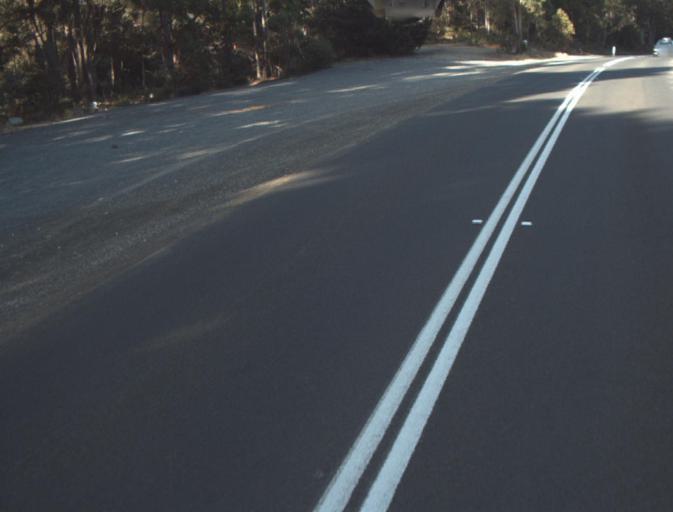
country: AU
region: Tasmania
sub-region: Launceston
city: Mayfield
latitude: -41.3367
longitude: 147.1695
